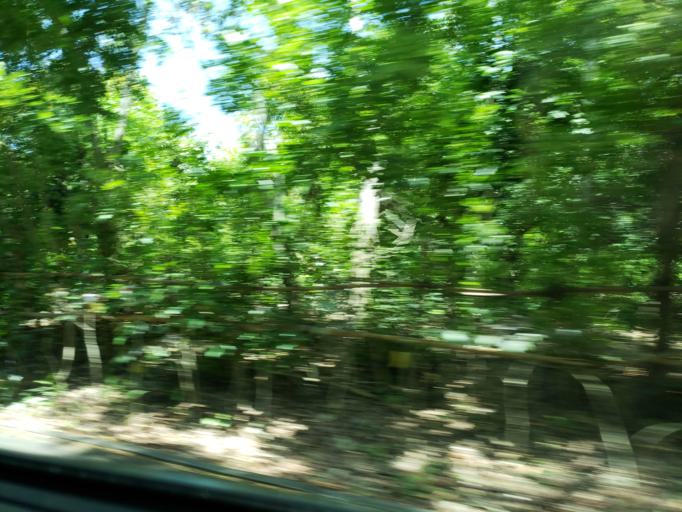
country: ID
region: Bali
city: Kangin
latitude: -8.8441
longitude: 115.1388
